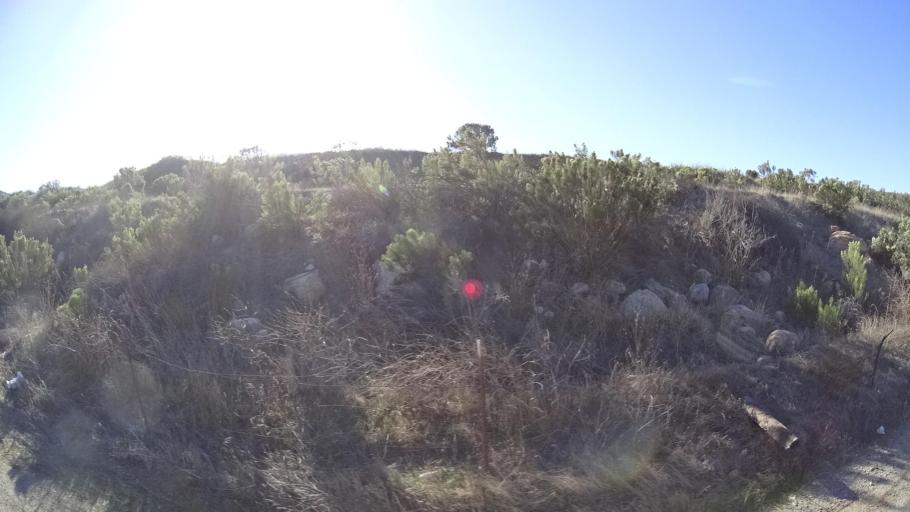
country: US
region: California
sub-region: San Diego County
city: Jamul
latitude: 32.6423
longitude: -116.8723
